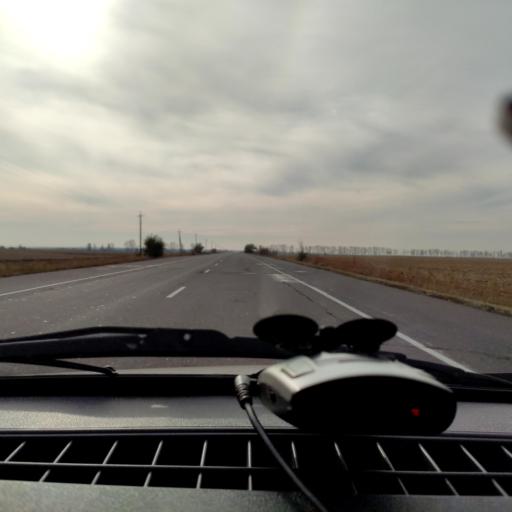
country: RU
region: Voronezj
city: Strelitsa
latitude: 51.5413
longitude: 38.9707
